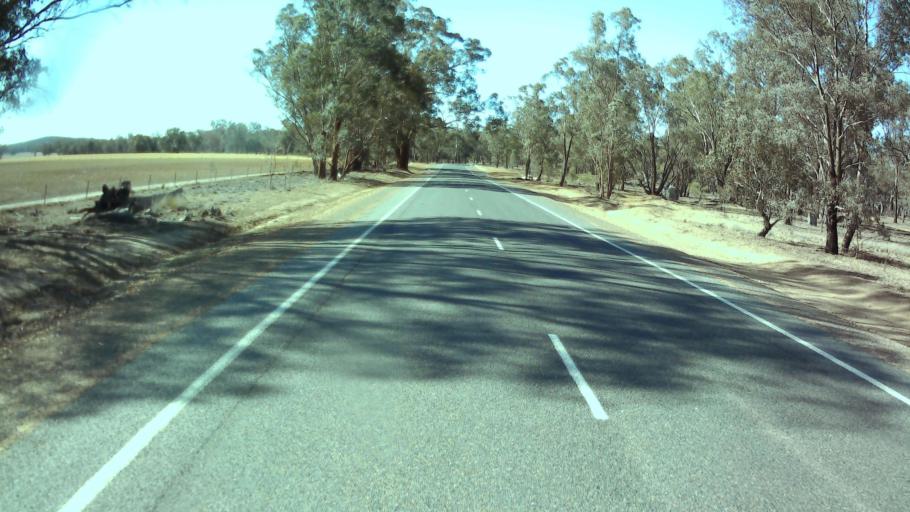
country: AU
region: New South Wales
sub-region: Weddin
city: Grenfell
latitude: -33.7667
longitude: 148.0826
